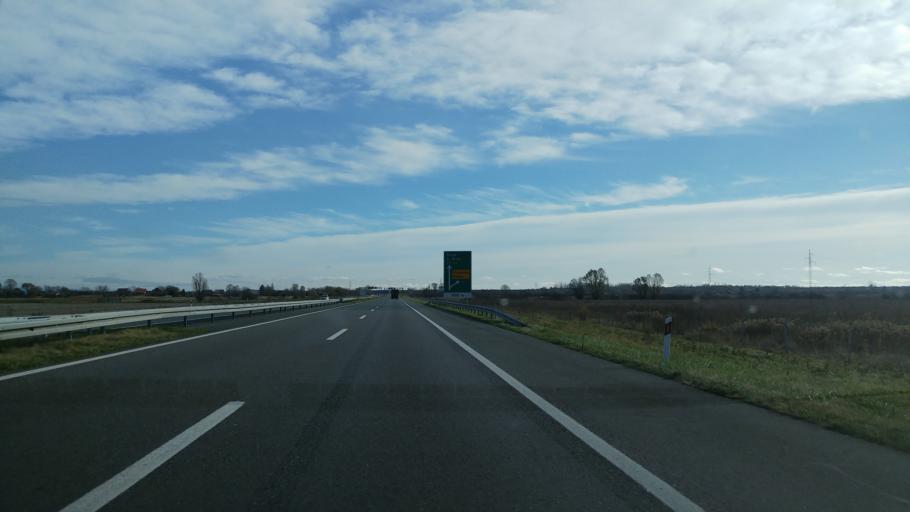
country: HR
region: Sisacko-Moslavacka
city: Repusnica
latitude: 45.4681
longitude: 16.7453
